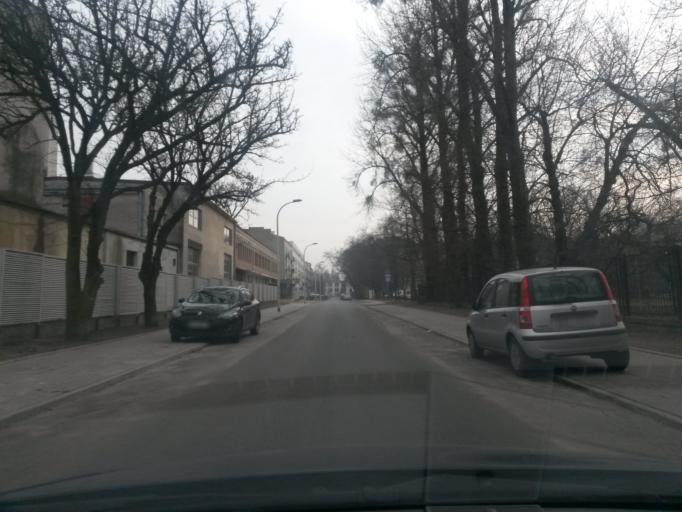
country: PL
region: Masovian Voivodeship
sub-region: Warszawa
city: Mokotow
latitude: 52.2050
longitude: 21.0426
